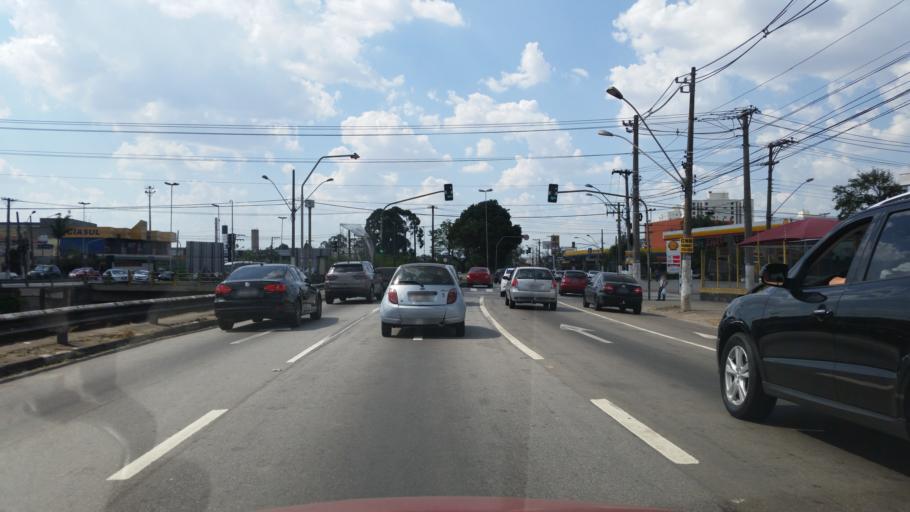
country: BR
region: Sao Paulo
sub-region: Sao Caetano Do Sul
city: Sao Caetano do Sul
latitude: -23.6252
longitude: -46.5408
